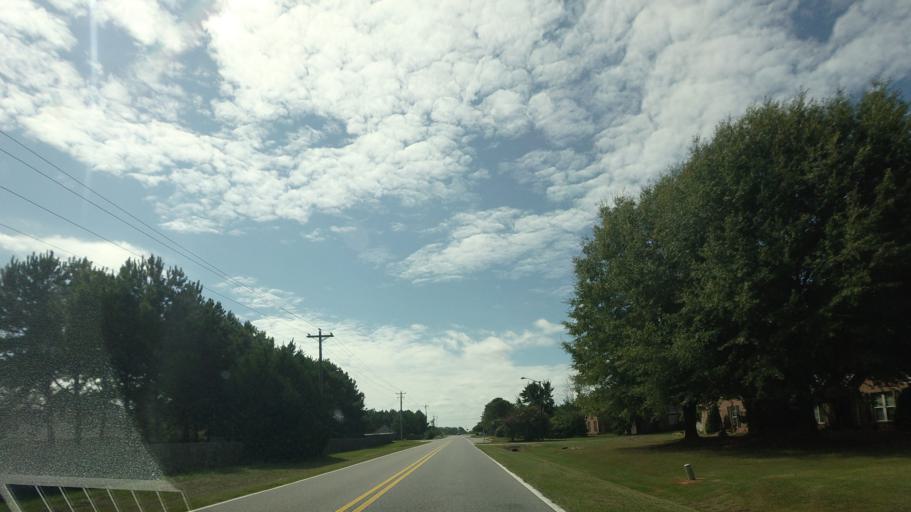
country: US
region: Georgia
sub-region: Houston County
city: Centerville
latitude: 32.5842
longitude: -83.7006
